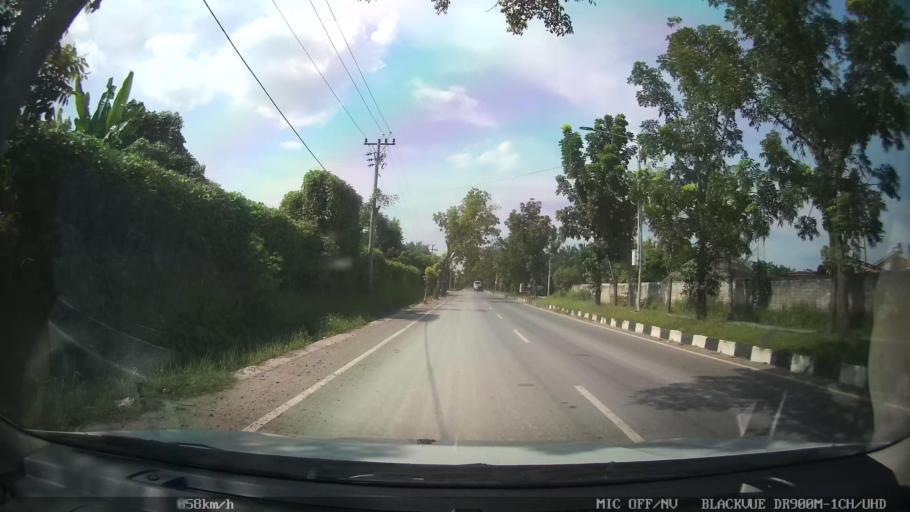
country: ID
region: North Sumatra
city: Binjai
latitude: 3.6343
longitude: 98.5351
